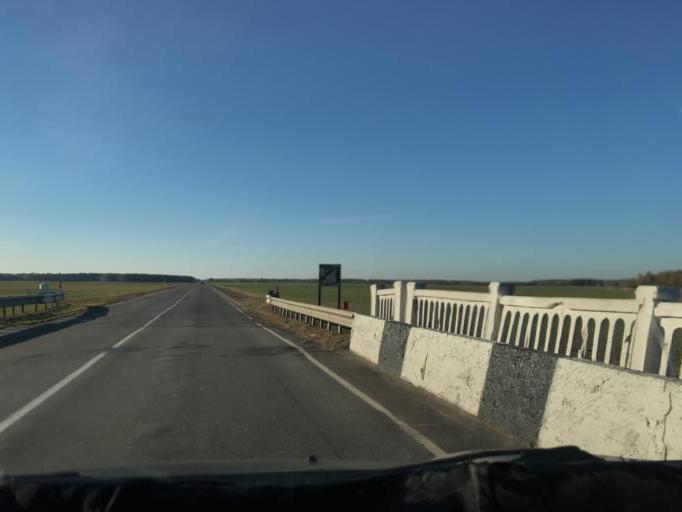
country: BY
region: Gomel
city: Mazyr
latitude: 52.2196
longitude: 29.0115
